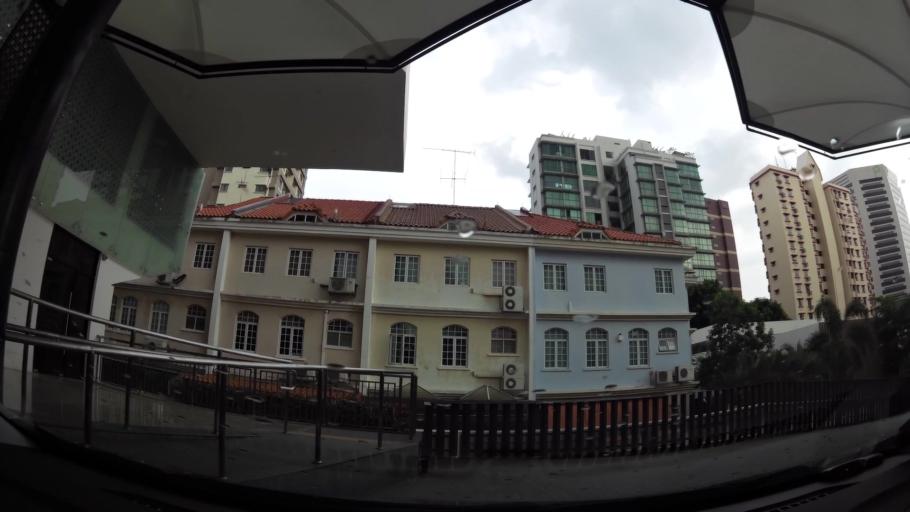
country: SG
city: Singapore
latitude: 1.3034
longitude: 103.9031
